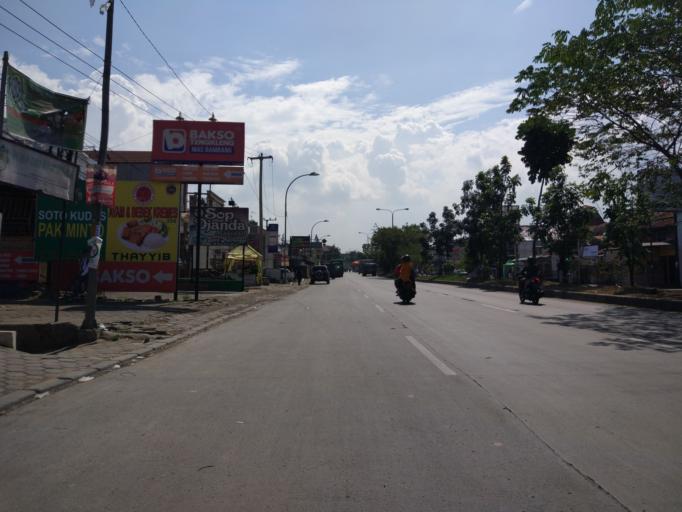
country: ID
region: West Java
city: Cileunyi
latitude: -6.9503
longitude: 107.7626
